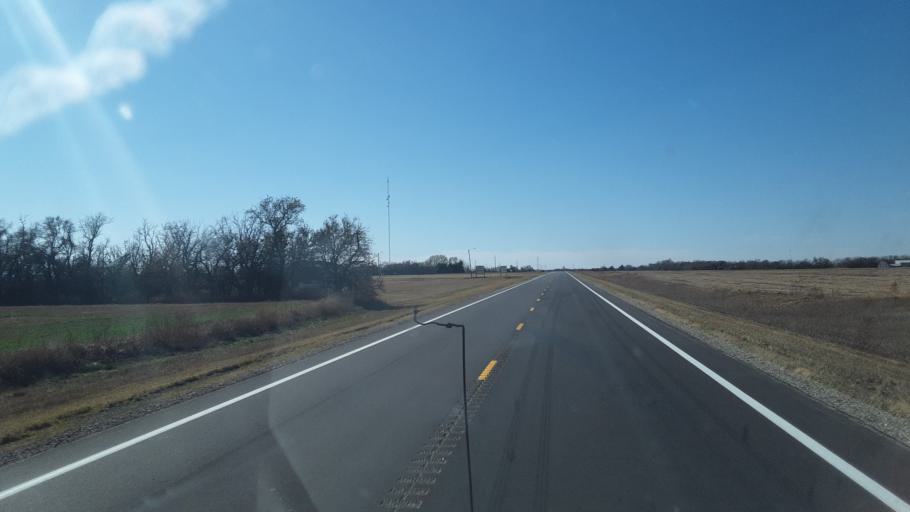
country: US
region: Kansas
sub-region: Rice County
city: Lyons
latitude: 38.3727
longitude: -98.1361
